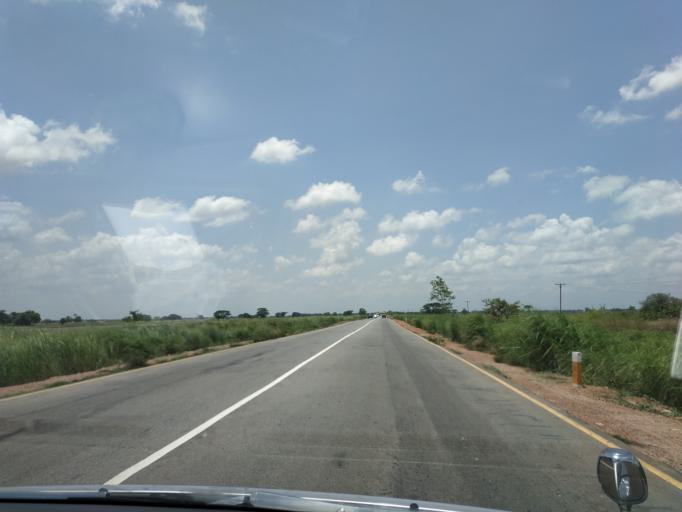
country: MM
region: Bago
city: Thanatpin
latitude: 17.4511
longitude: 96.6337
